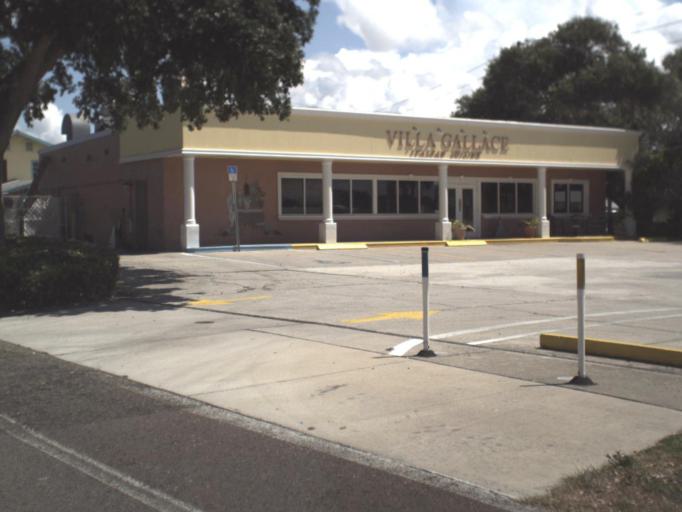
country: US
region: Florida
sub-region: Pinellas County
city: Indian Rocks Beach
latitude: 27.8786
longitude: -82.8503
